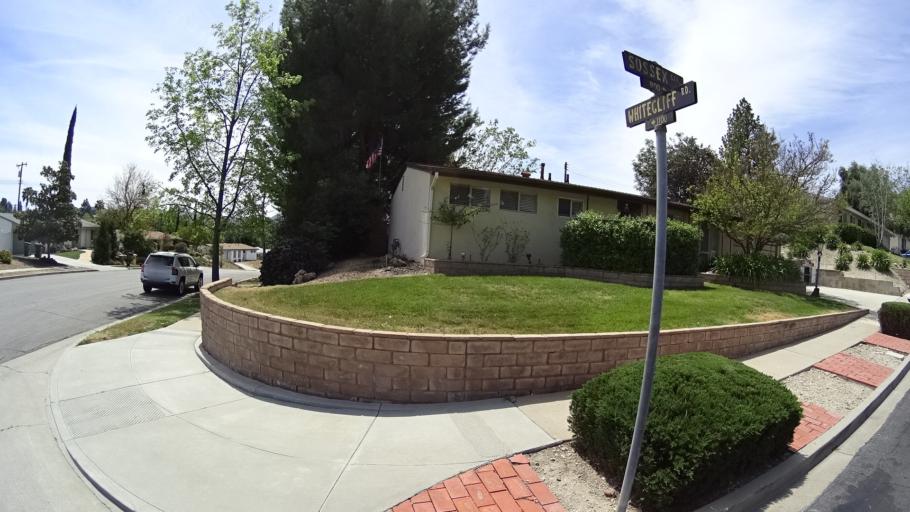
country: US
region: California
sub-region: Ventura County
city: Thousand Oaks
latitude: 34.1939
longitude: -118.8623
